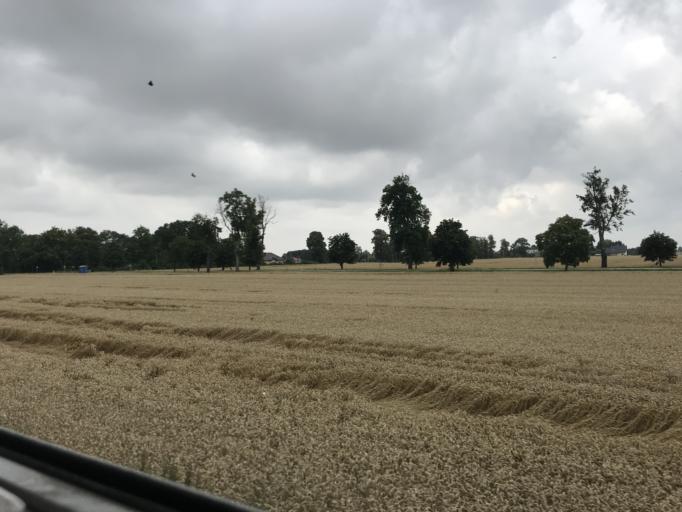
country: PL
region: Pomeranian Voivodeship
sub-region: Powiat malborski
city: Stare Pole
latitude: 54.0451
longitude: 19.1640
